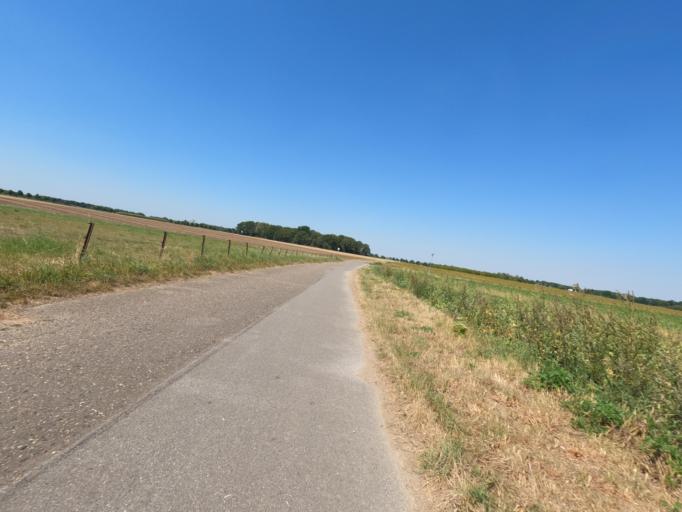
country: DE
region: North Rhine-Westphalia
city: Wegberg
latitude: 51.1075
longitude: 6.2509
